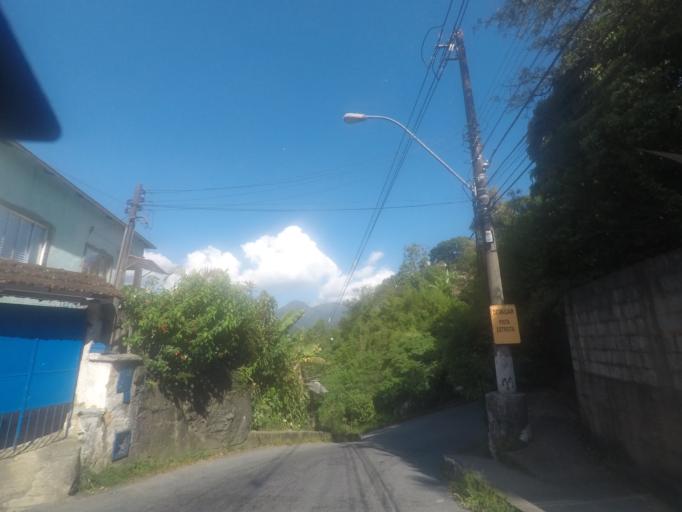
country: BR
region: Rio de Janeiro
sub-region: Petropolis
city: Petropolis
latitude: -22.5222
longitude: -43.1983
